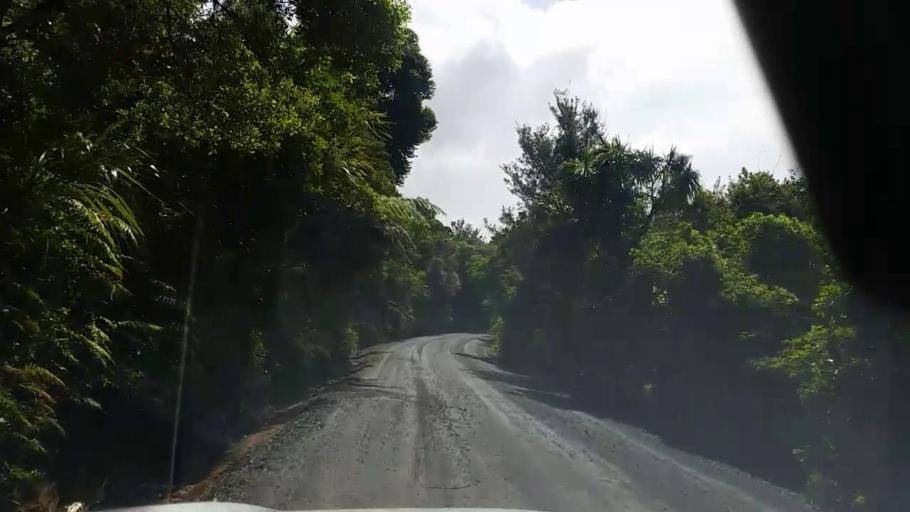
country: NZ
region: Auckland
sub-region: Auckland
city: Muriwai Beach
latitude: -36.9371
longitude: 174.5151
